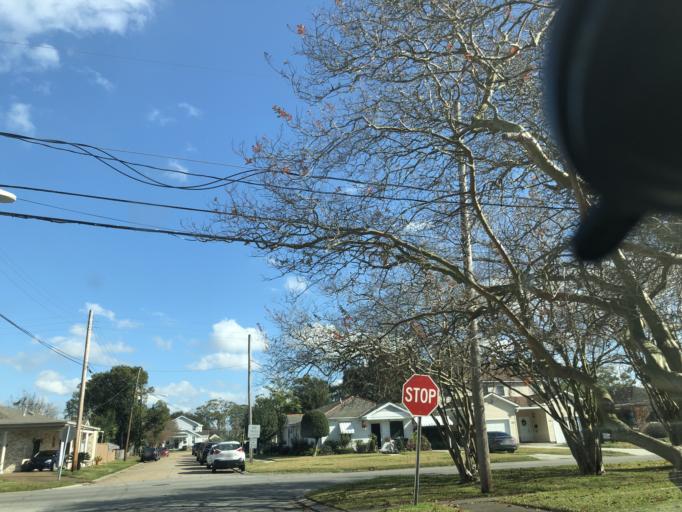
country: US
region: Louisiana
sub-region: Jefferson Parish
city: Metairie Terrace
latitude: 29.9799
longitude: -90.1608
